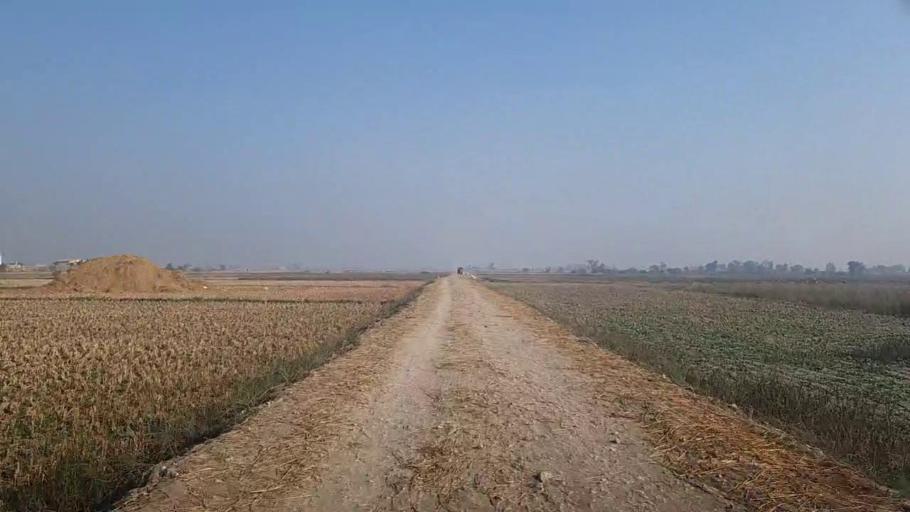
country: PK
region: Sindh
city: Radhan
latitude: 27.1433
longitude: 67.9091
